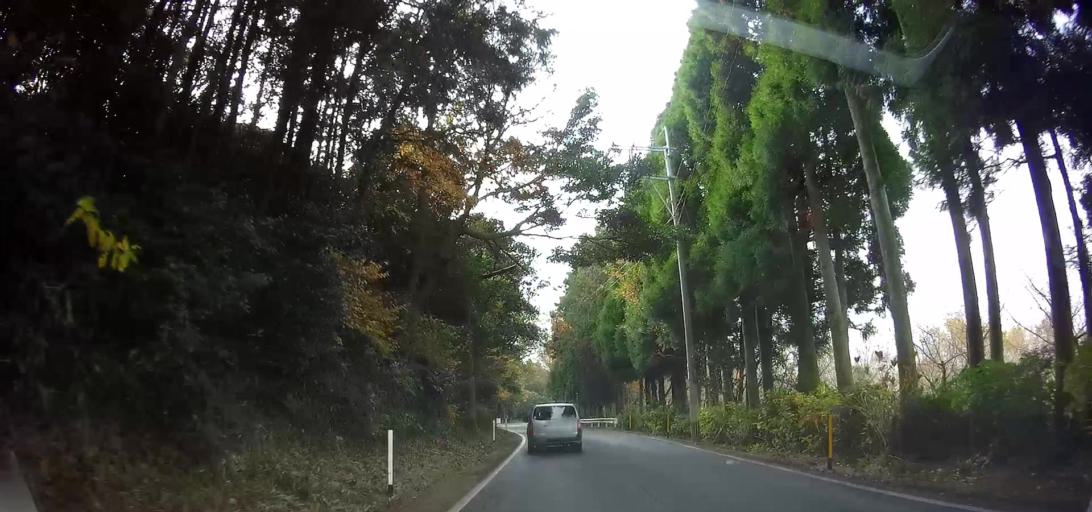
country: JP
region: Nagasaki
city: Shimabara
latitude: 32.6997
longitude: 130.2480
